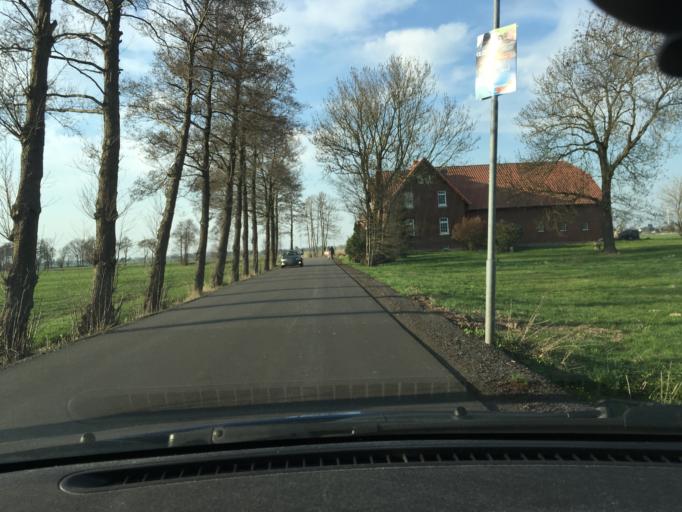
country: DE
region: Lower Saxony
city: Stelle
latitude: 53.4357
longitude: 10.0645
